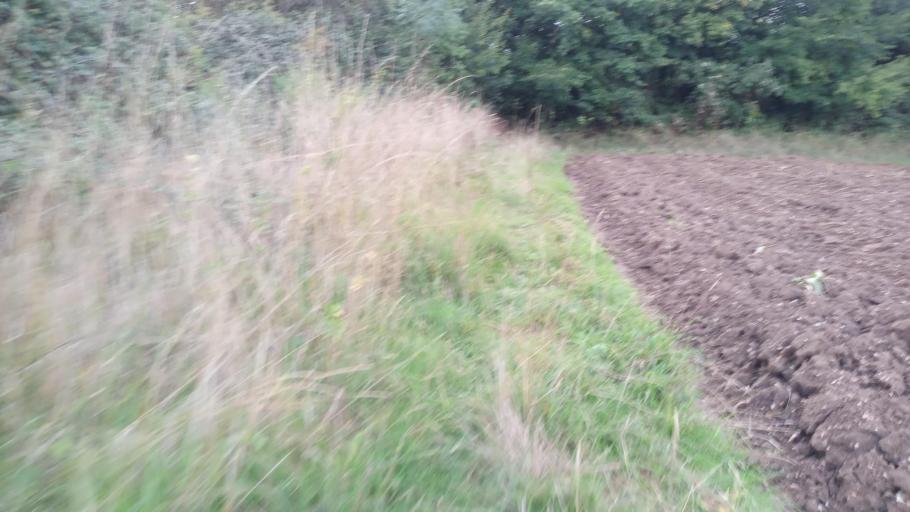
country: GB
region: England
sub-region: Cambridgeshire
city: Linton
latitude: 52.0552
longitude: 0.3088
